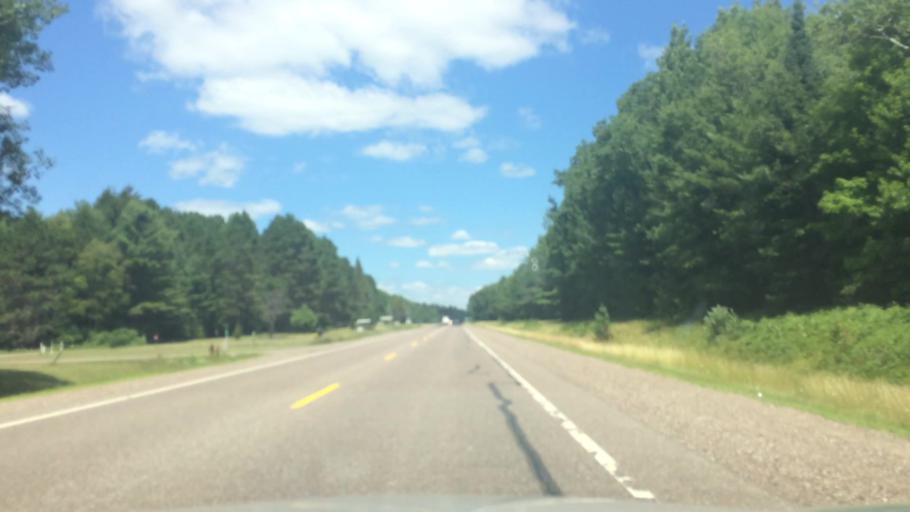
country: US
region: Wisconsin
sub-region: Vilas County
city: Lac du Flambeau
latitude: 45.9745
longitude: -89.6993
